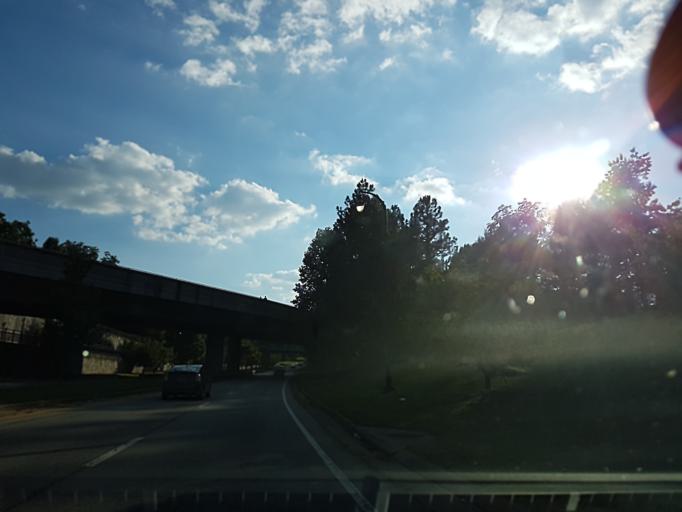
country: US
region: Georgia
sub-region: Fulton County
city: Atlanta
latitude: 33.7618
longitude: -84.3661
